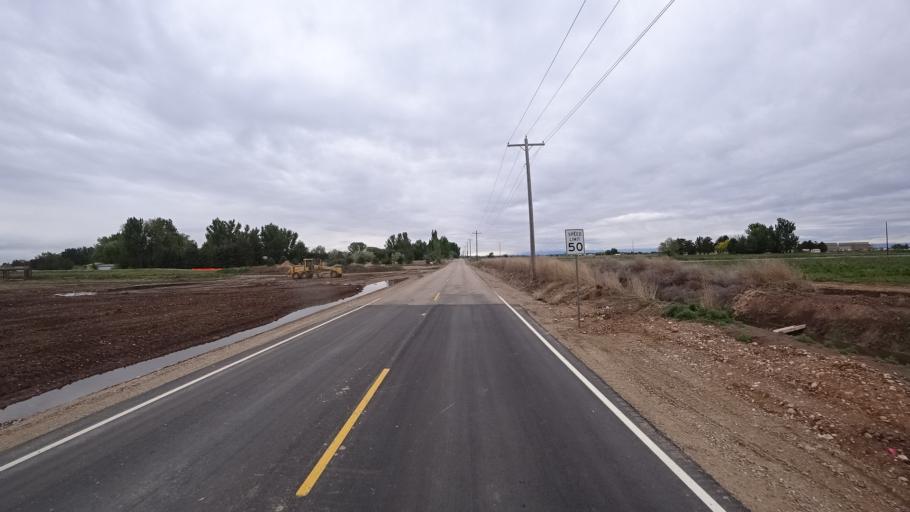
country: US
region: Idaho
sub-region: Ada County
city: Star
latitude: 43.6435
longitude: -116.4735
